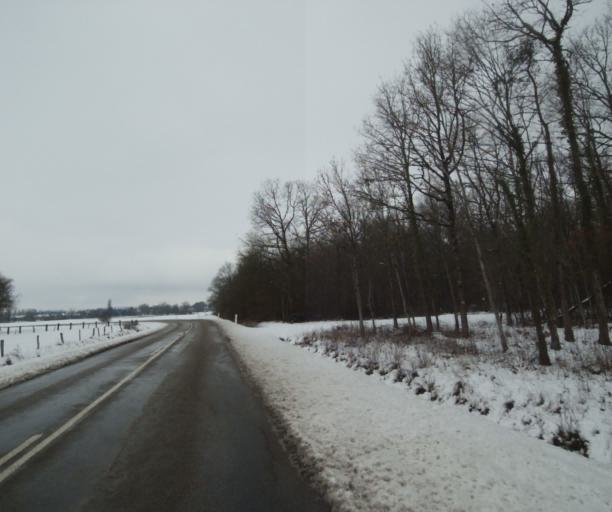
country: FR
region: Champagne-Ardenne
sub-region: Departement de la Haute-Marne
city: Montier-en-Der
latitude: 48.4795
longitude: 4.7907
